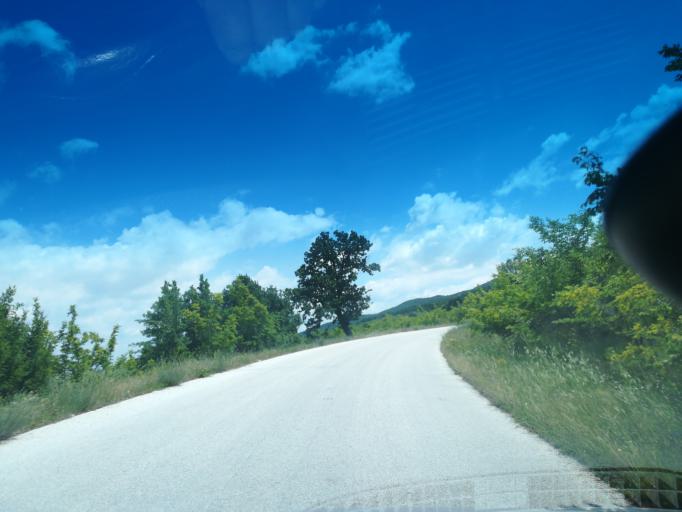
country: BG
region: Khaskovo
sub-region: Obshtina Mineralni Bani
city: Mineralni Bani
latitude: 41.9794
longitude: 25.2488
